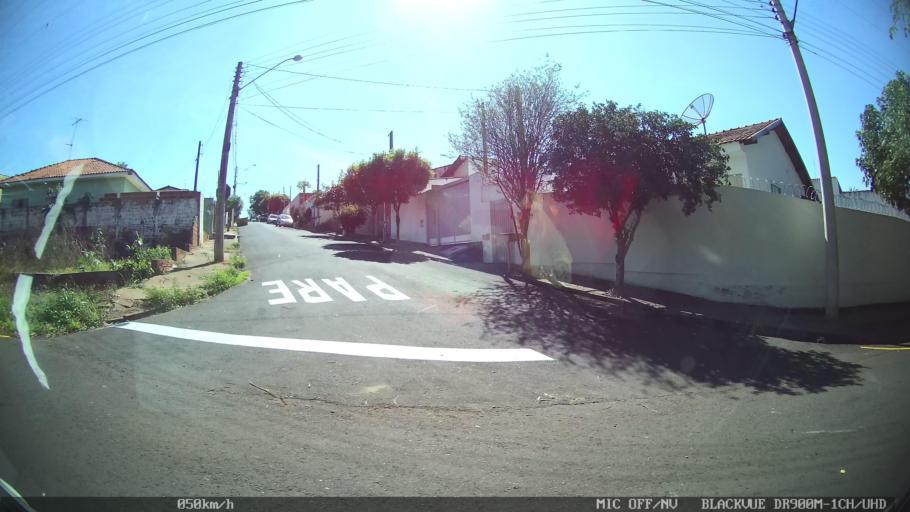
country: BR
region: Sao Paulo
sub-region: Sao Jose Do Rio Preto
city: Sao Jose do Rio Preto
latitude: -20.7727
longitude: -49.4050
